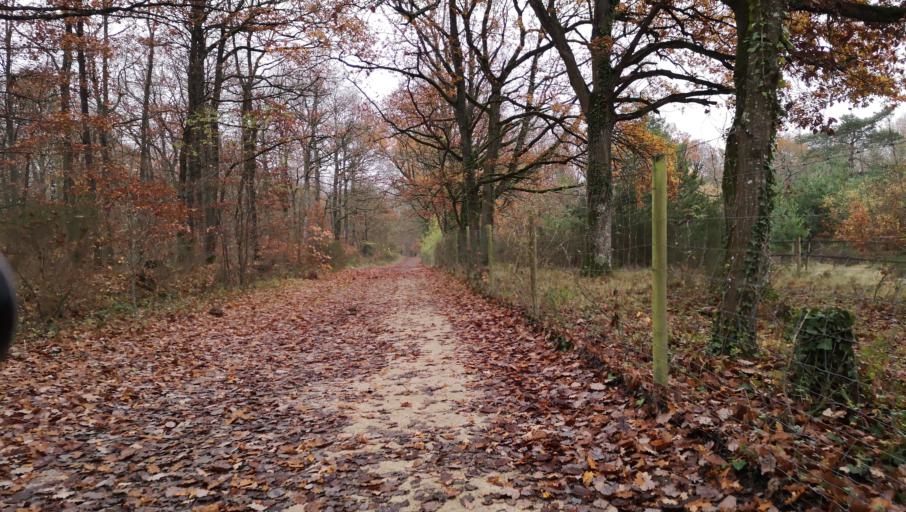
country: FR
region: Centre
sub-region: Departement du Loiret
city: Semoy
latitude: 47.9393
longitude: 1.9721
